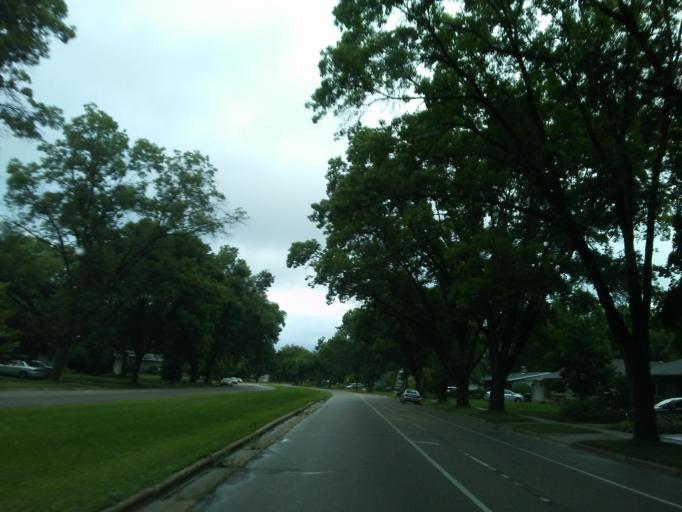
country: US
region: Wisconsin
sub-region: Dane County
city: Shorewood Hills
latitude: 43.0655
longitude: -89.4543
